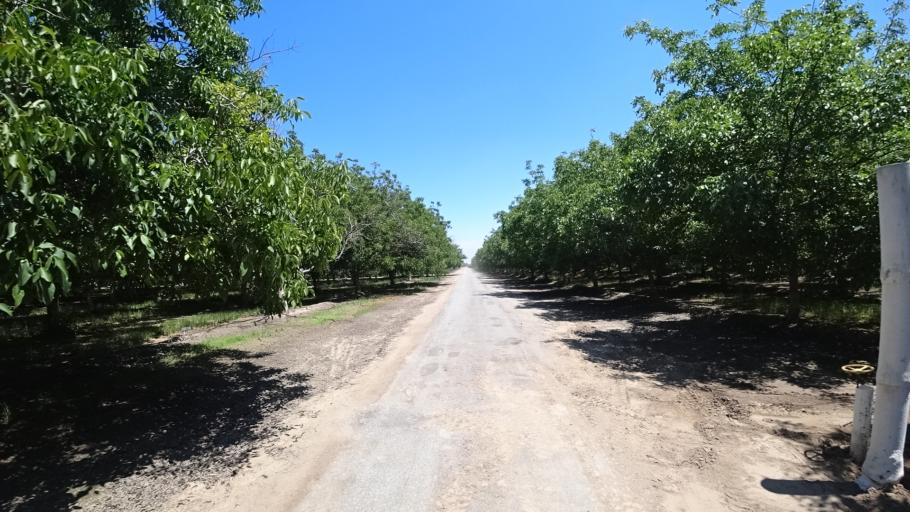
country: US
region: California
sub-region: Kings County
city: Lucerne
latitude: 36.4230
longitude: -119.6153
